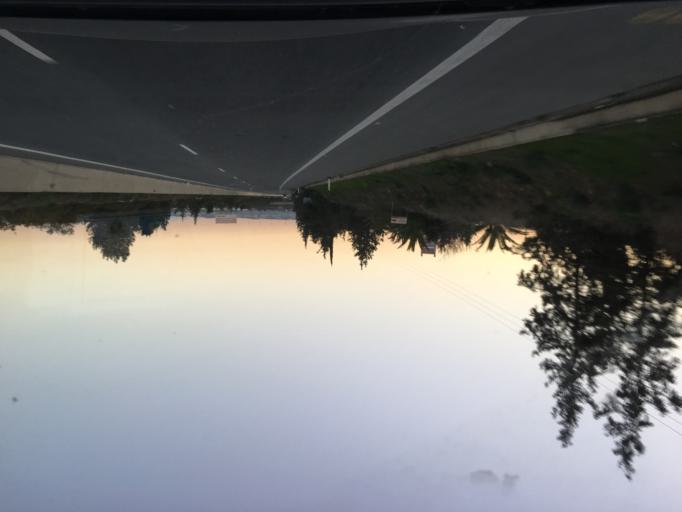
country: CY
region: Larnaka
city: Dhromolaxia
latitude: 34.8858
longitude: 33.5896
